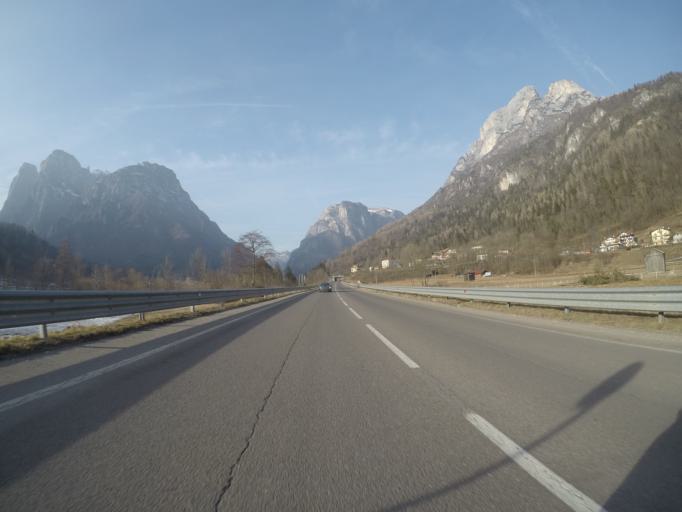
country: IT
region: Veneto
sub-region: Provincia di Belluno
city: Taibon Agordino
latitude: 46.2921
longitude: 12.0204
